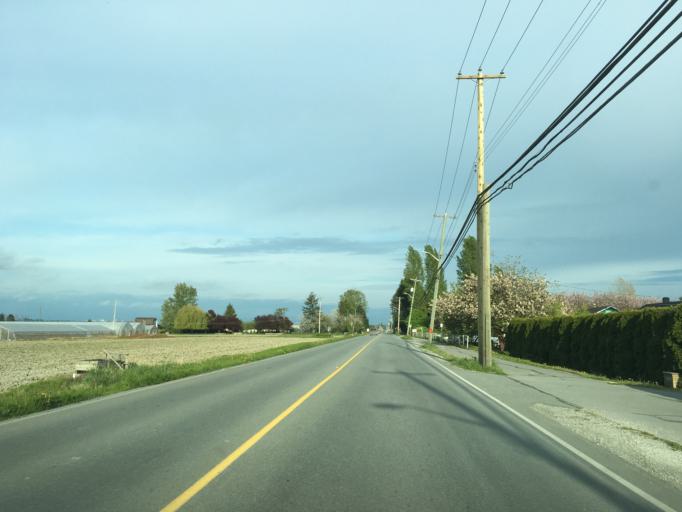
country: CA
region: British Columbia
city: Richmond
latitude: 49.1699
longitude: -123.0559
